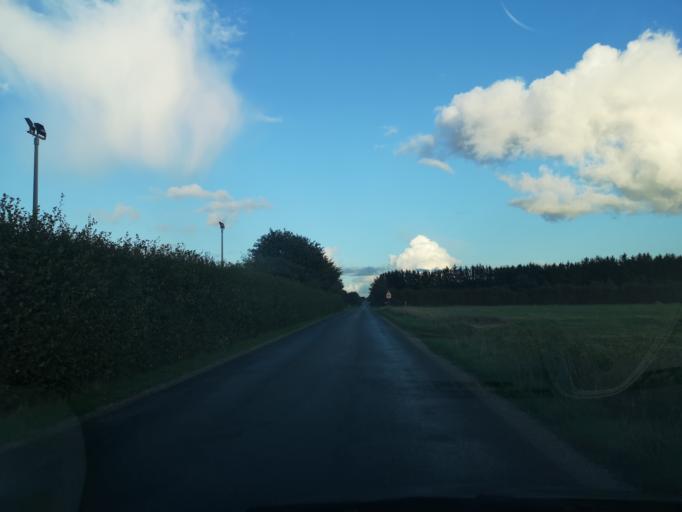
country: DK
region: Central Jutland
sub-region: Ringkobing-Skjern Kommune
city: Skjern
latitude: 56.0224
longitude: 8.5507
